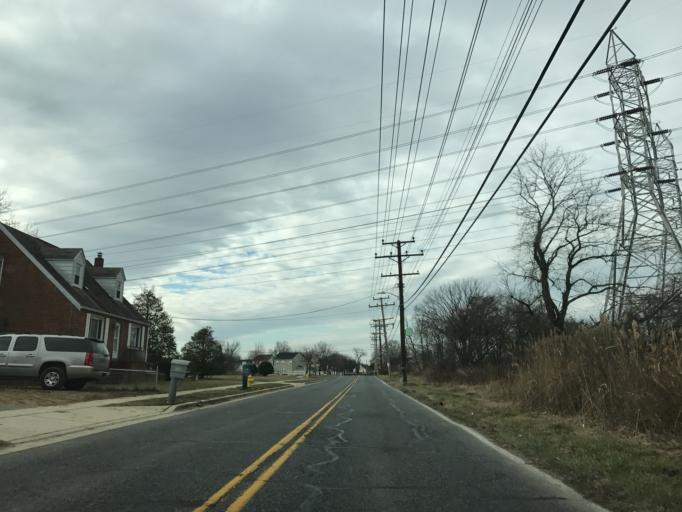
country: US
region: Maryland
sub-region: Anne Arundel County
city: Pumphrey
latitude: 39.2109
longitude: -76.6314
